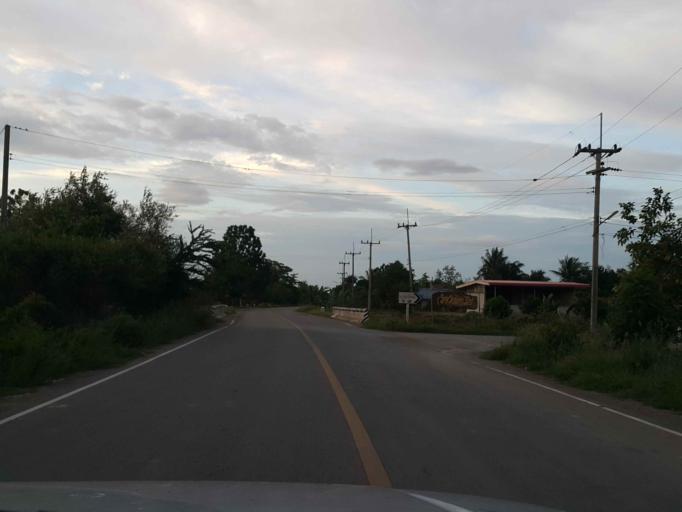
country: TH
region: Sukhothai
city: Ban Dan Lan Hoi
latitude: 17.1079
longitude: 99.5939
